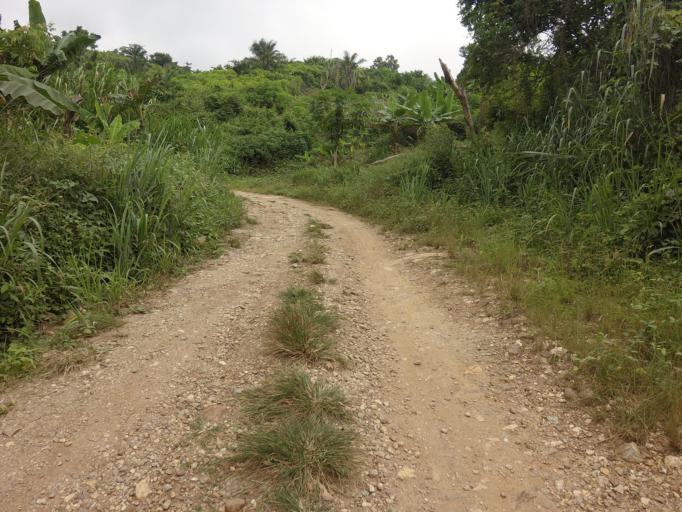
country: GH
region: Volta
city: Kpandu
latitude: 6.8740
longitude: 0.4408
